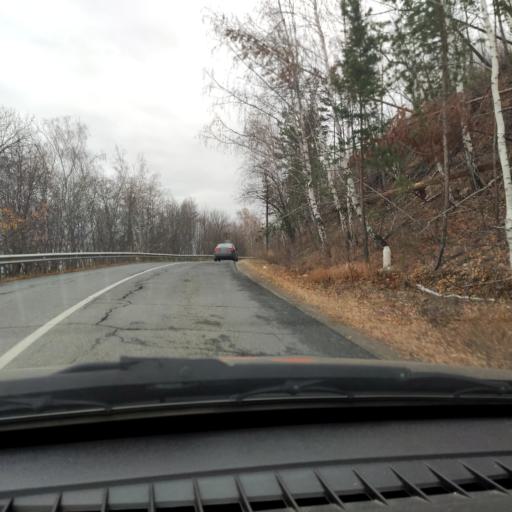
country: RU
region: Samara
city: Pribrezhnyy
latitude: 53.4418
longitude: 49.7741
